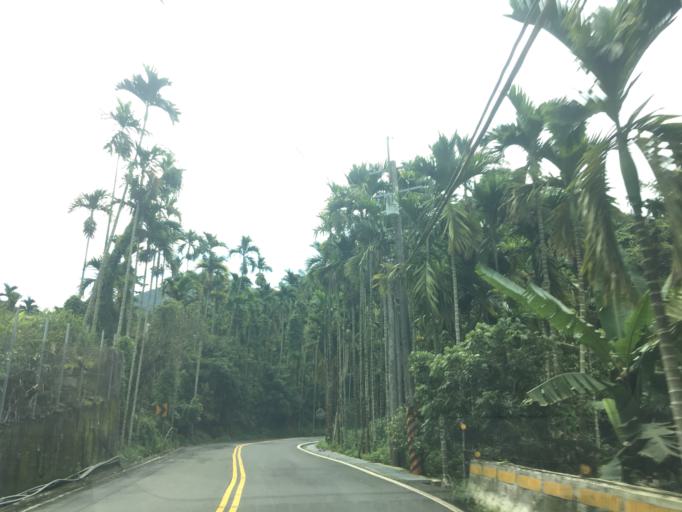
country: TW
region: Taiwan
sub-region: Yunlin
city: Douliu
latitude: 23.5634
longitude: 120.5756
